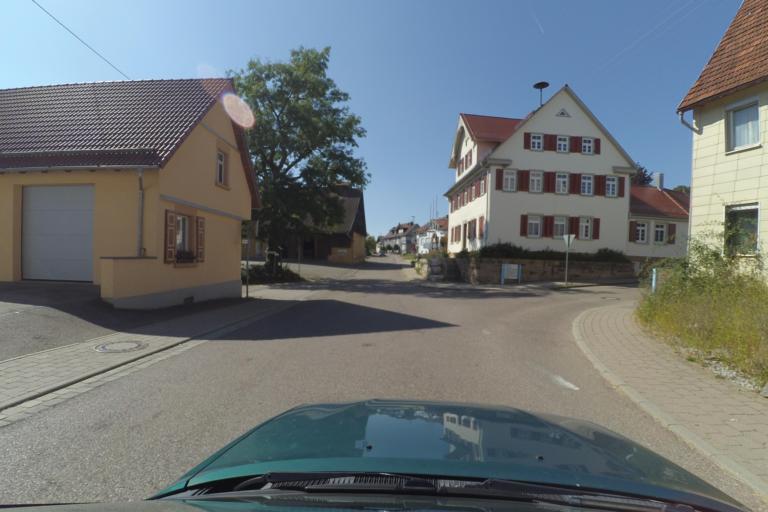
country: DE
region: Baden-Wuerttemberg
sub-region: Regierungsbezirk Stuttgart
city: Ruppertshofen
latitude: 48.8839
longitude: 9.8156
